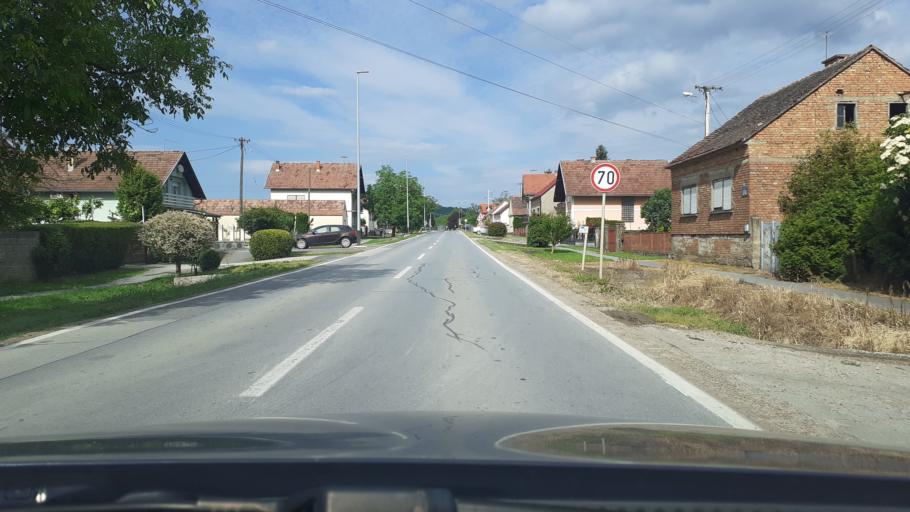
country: HR
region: Brodsko-Posavska
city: Sibinj
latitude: 45.1845
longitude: 17.8921
